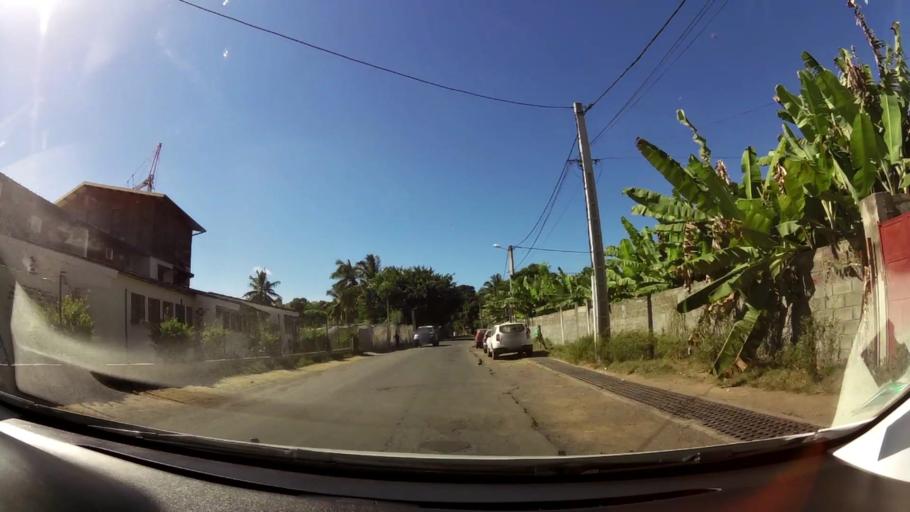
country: YT
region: Pamandzi
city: Pamandzi
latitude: -12.7804
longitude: 45.2803
